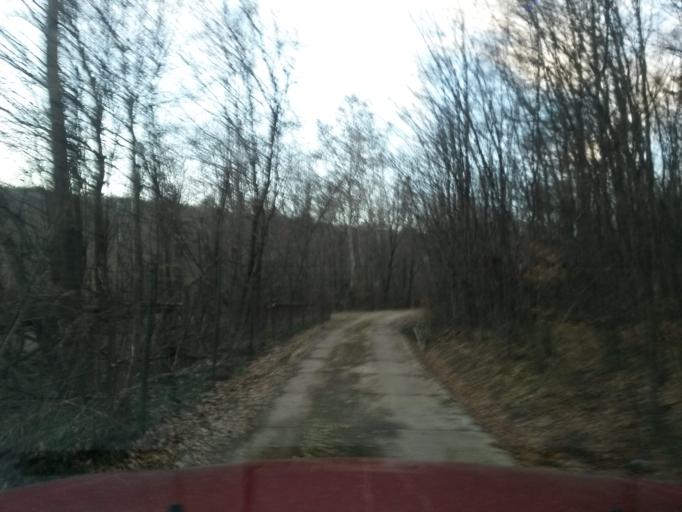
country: SK
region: Kosicky
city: Kosice
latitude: 48.6943
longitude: 21.3045
